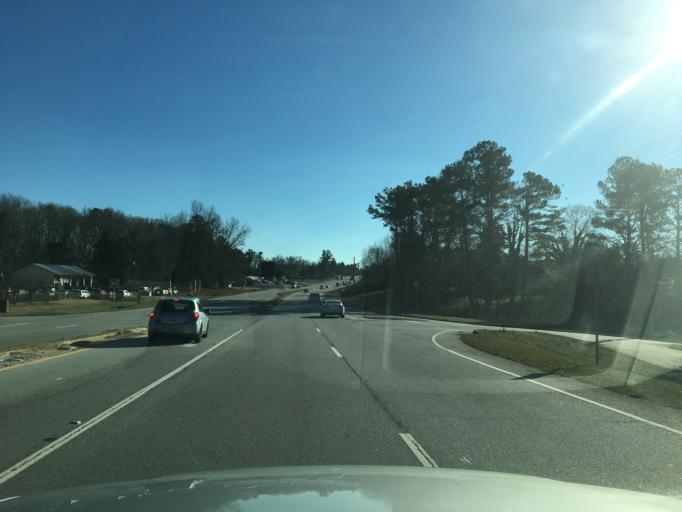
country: US
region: Georgia
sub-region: Carroll County
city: Carrollton
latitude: 33.5275
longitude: -85.0746
